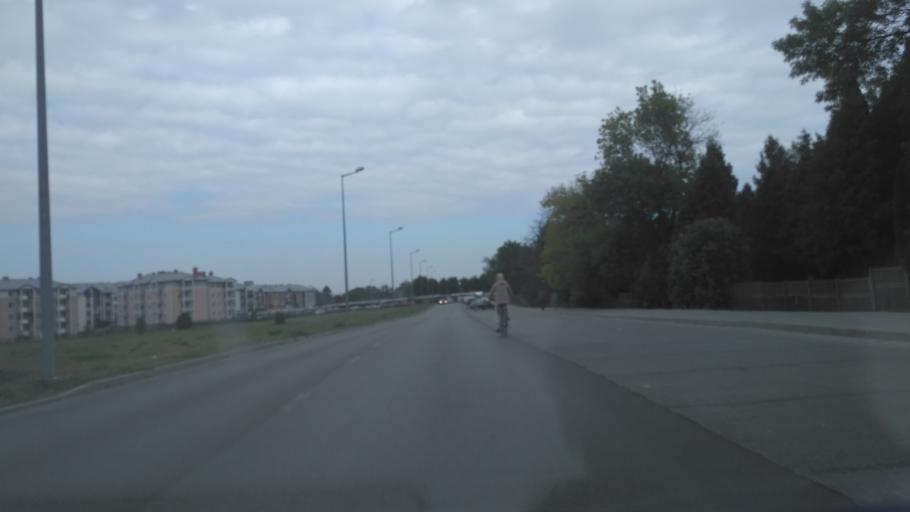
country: PL
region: Lublin Voivodeship
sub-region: Chelm
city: Chelm
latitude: 51.1269
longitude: 23.4655
